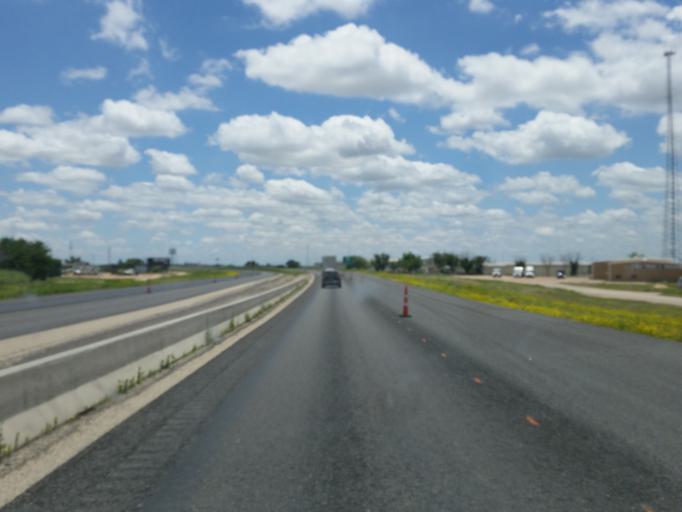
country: US
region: Texas
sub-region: Scurry County
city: Snyder
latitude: 32.7447
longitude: -100.9231
